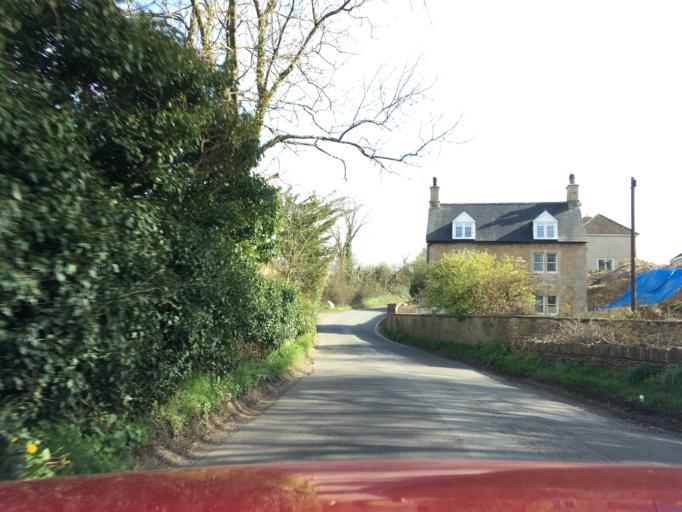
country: GB
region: England
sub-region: Wiltshire
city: Chippenham
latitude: 51.4937
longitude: -2.1380
